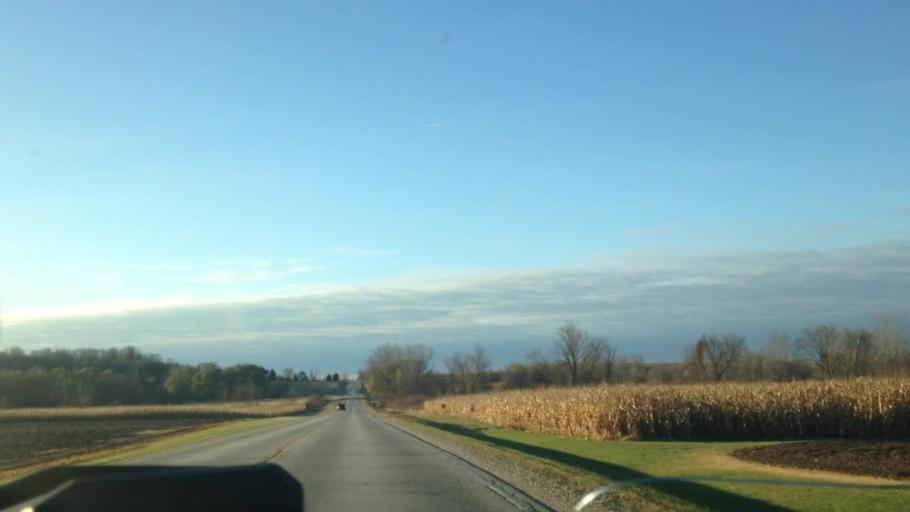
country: US
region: Wisconsin
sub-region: Dodge County
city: Mayville
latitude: 43.4516
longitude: -88.4999
